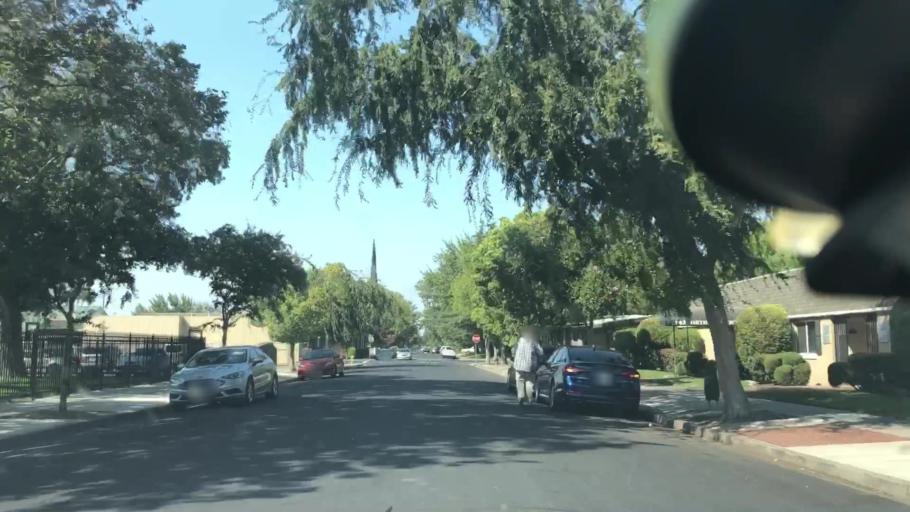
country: US
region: California
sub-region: San Joaquin County
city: Manteca
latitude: 37.7982
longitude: -121.2153
